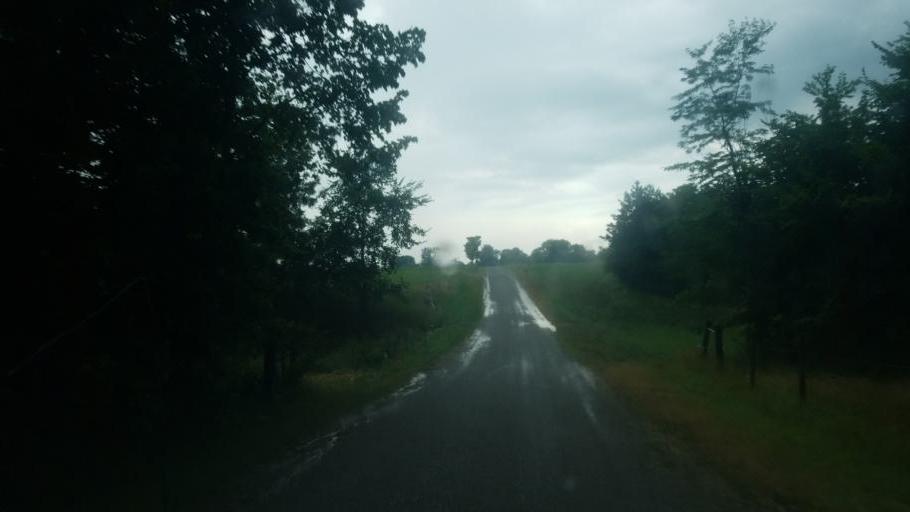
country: US
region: Indiana
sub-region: DeKalb County
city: Butler
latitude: 41.4627
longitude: -84.8234
